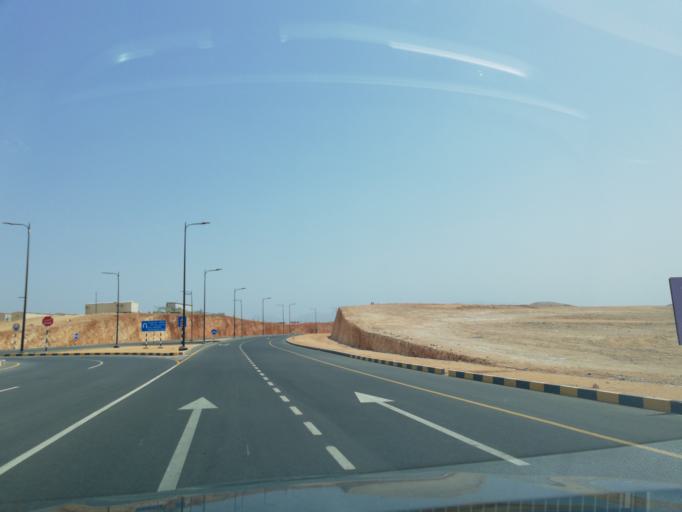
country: OM
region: Muhafazat Masqat
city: Bawshar
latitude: 23.5673
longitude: 58.3211
